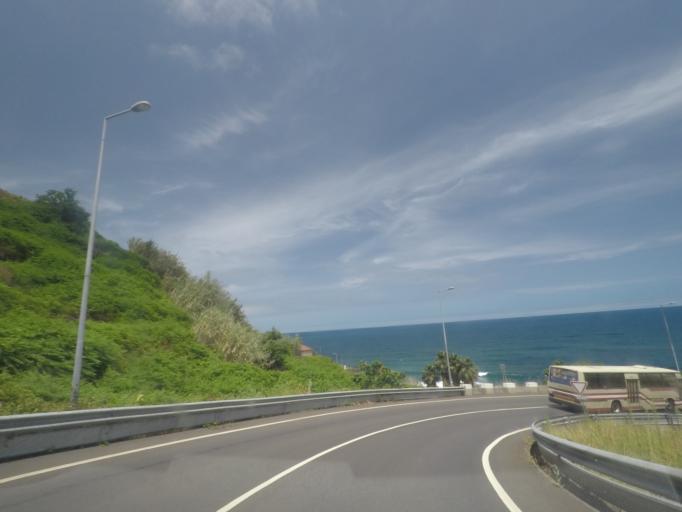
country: PT
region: Madeira
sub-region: Sao Vicente
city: Sao Vicente
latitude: 32.8139
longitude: -17.0239
